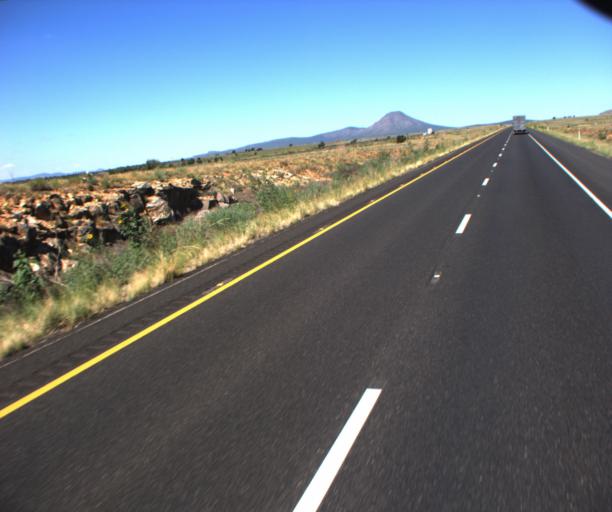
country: US
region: Arizona
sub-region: Yavapai County
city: Paulden
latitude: 35.2341
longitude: -112.6211
